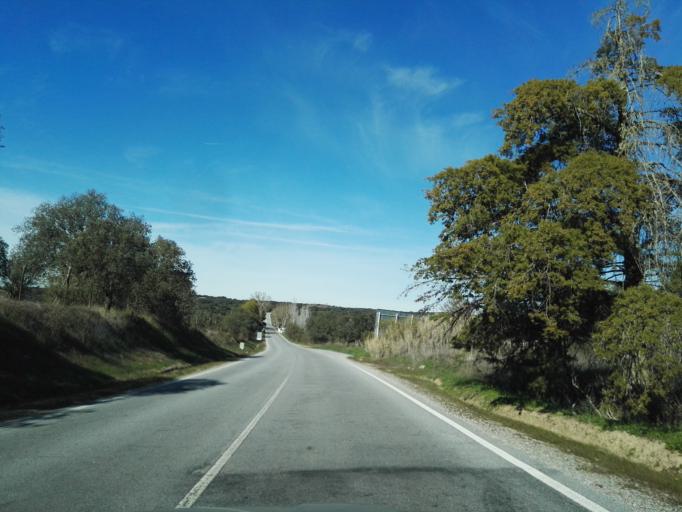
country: PT
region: Portalegre
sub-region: Arronches
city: Arronches
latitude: 39.0538
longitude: -7.2688
